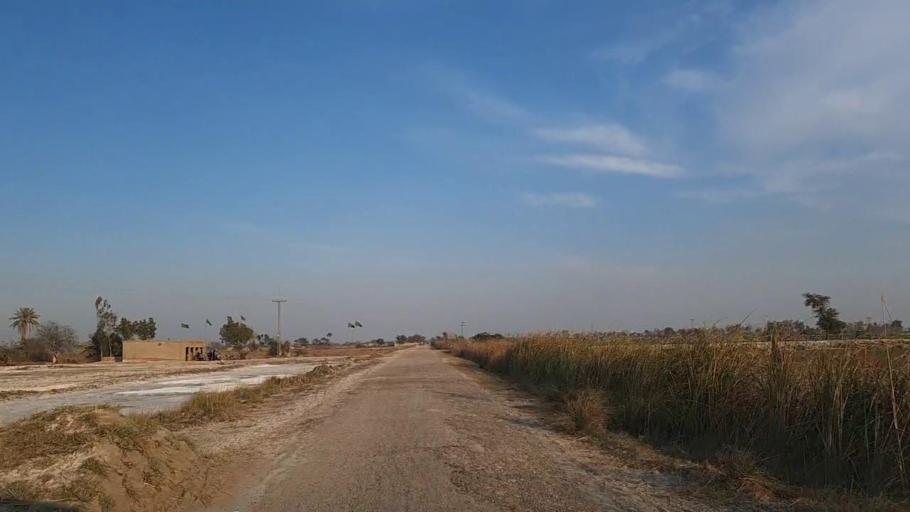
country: PK
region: Sindh
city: Bandhi
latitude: 26.5745
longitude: 68.3382
